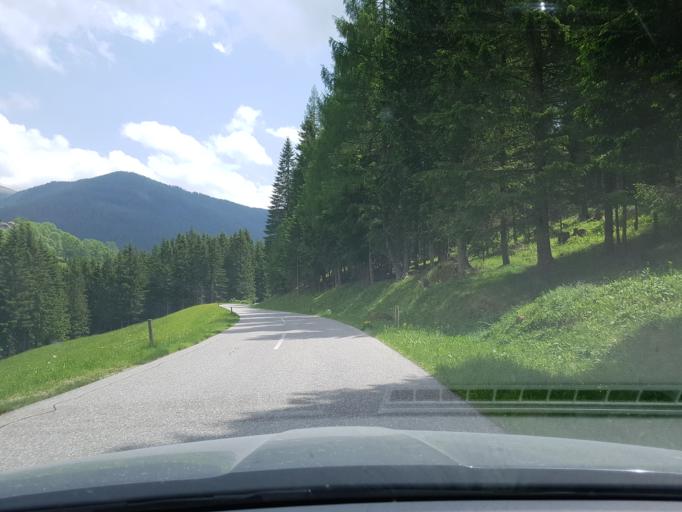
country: AT
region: Carinthia
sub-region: Politischer Bezirk Spittal an der Drau
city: Kleinkirchheim
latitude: 46.8746
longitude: 13.8662
